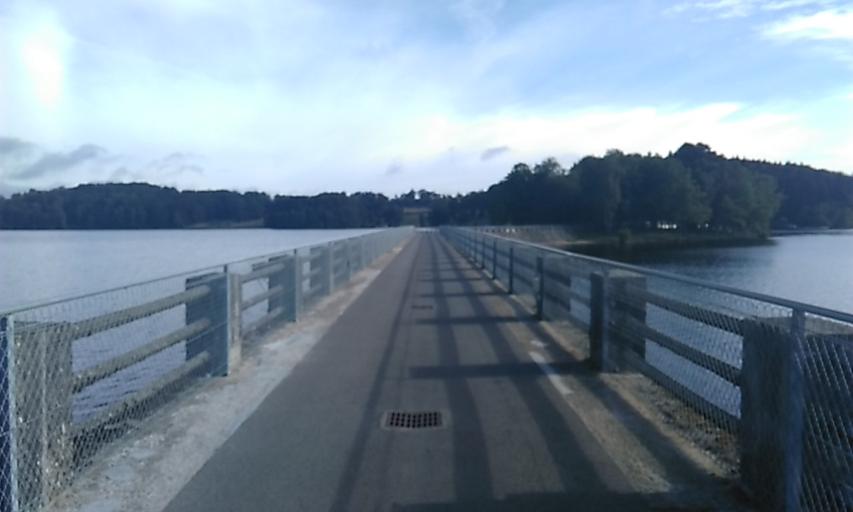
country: FR
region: Limousin
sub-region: Departement de la Haute-Vienne
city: Peyrat-le-Chateau
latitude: 45.7936
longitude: 1.8622
